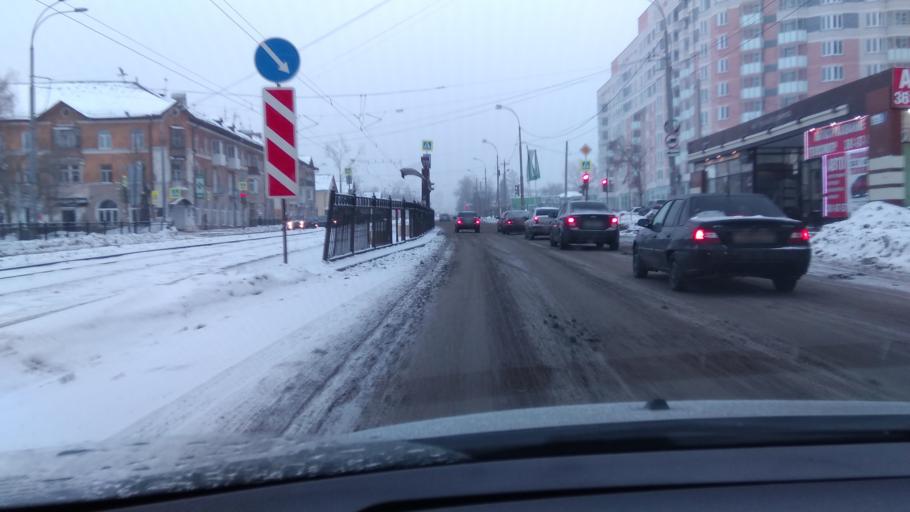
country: RU
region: Sverdlovsk
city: Yekaterinburg
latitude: 56.9024
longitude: 60.5840
